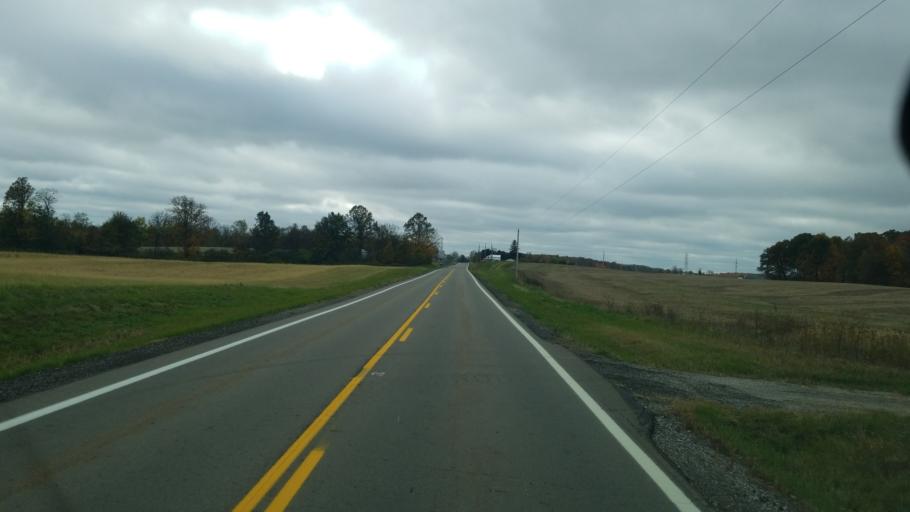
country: US
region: Ohio
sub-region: Richland County
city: Shelby
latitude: 40.8956
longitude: -82.7471
